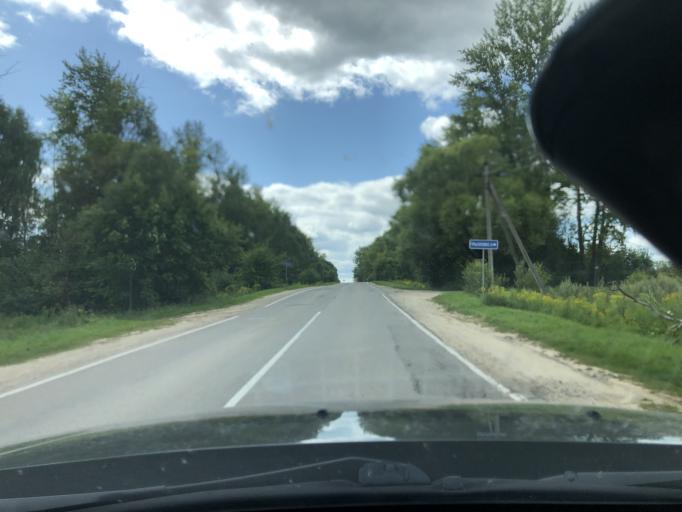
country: RU
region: Tula
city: Revyakino
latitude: 54.3512
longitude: 37.6267
